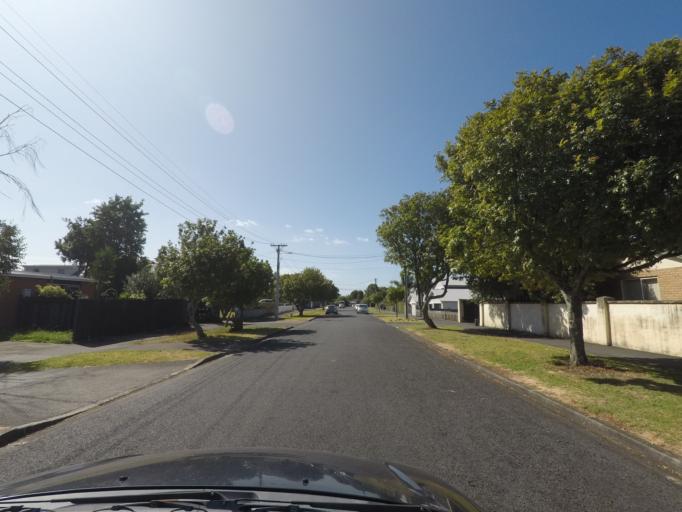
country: NZ
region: Auckland
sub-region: Auckland
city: Rosebank
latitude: -36.8927
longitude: 174.6937
